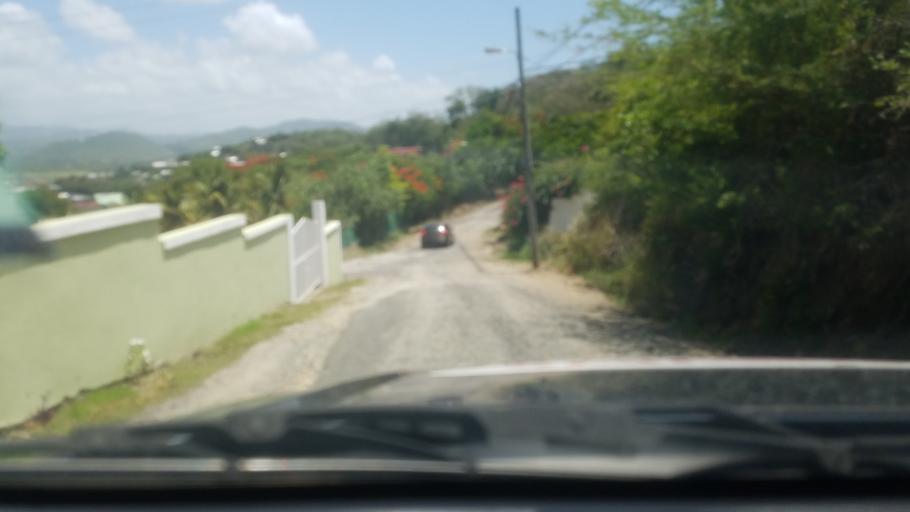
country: LC
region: Vieux-Fort
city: Vieux Fort
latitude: 13.7177
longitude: -60.9502
